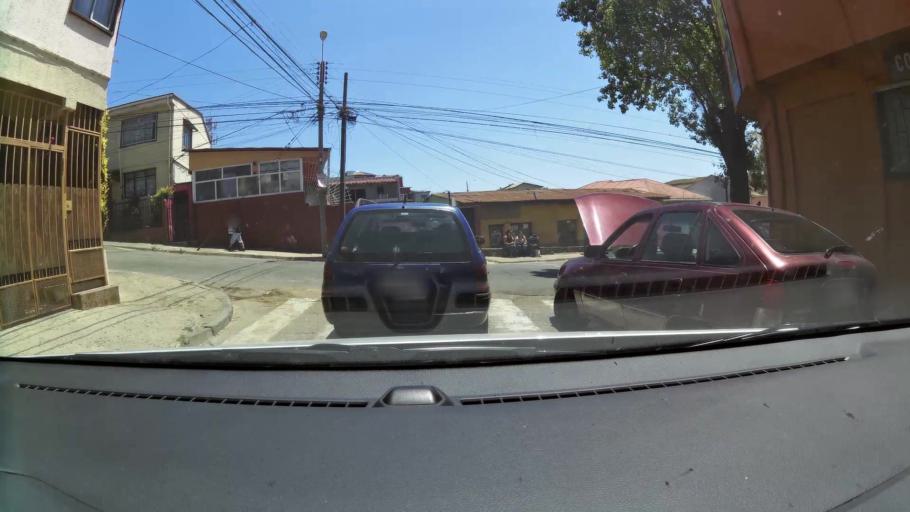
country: CL
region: Valparaiso
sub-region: Provincia de Valparaiso
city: Valparaiso
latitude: -33.0341
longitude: -71.6389
